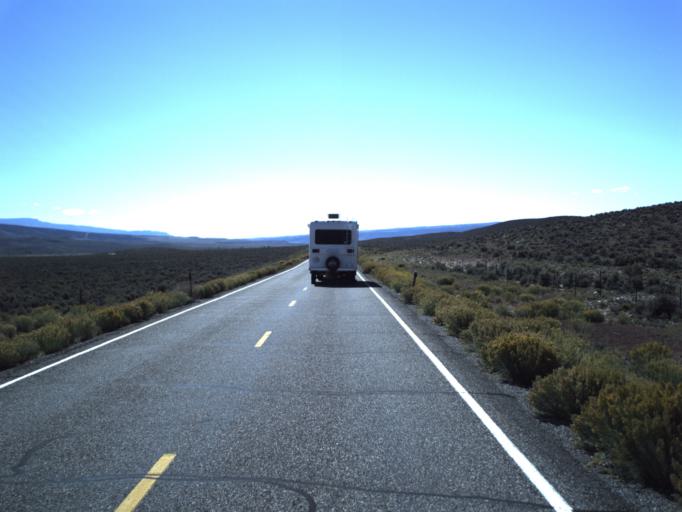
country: US
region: Utah
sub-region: Piute County
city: Junction
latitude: 38.2428
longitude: -111.9880
